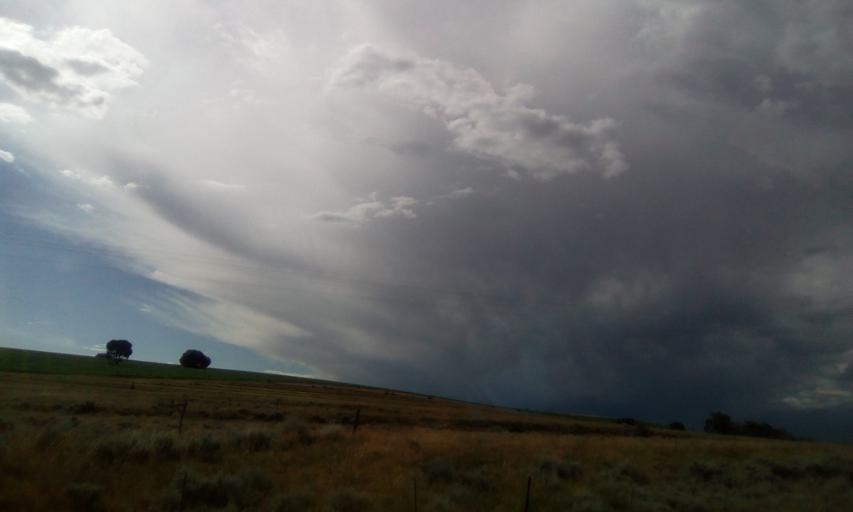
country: ZA
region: Orange Free State
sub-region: Thabo Mofutsanyana District Municipality
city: Ladybrand
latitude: -29.2359
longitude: 27.4494
